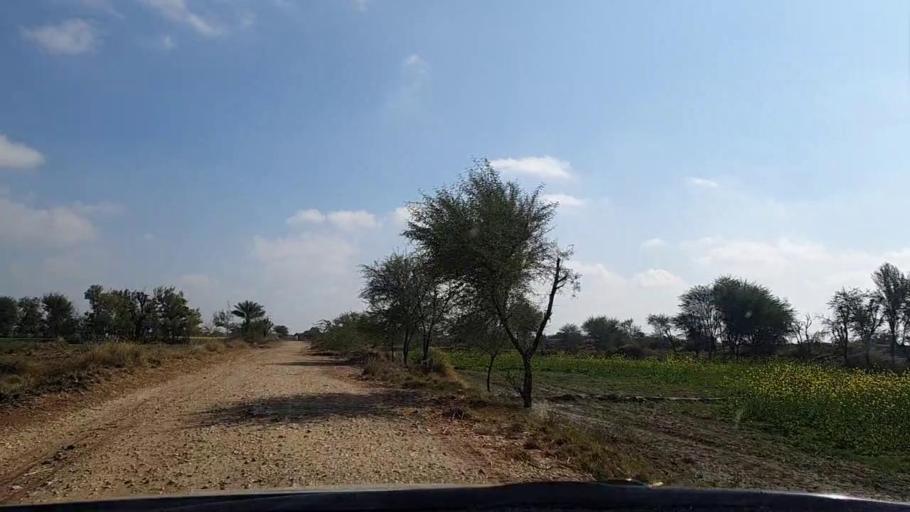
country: PK
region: Sindh
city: Tando Mittha Khan
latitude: 25.7408
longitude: 69.2405
